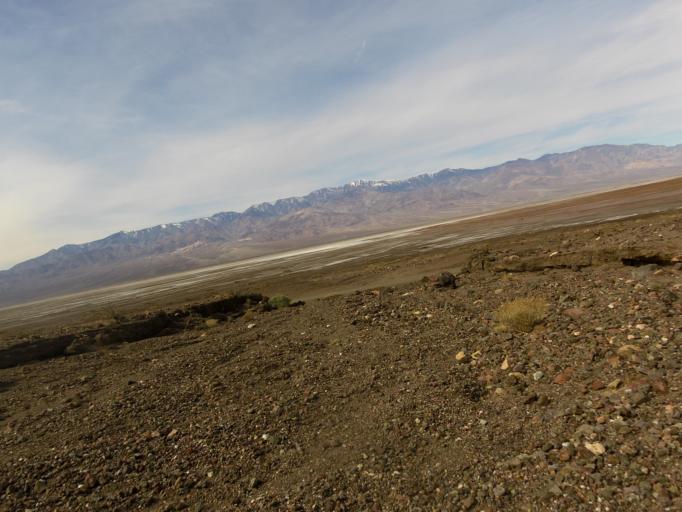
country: US
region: California
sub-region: San Bernardino County
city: Searles Valley
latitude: 36.1429
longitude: -116.7642
